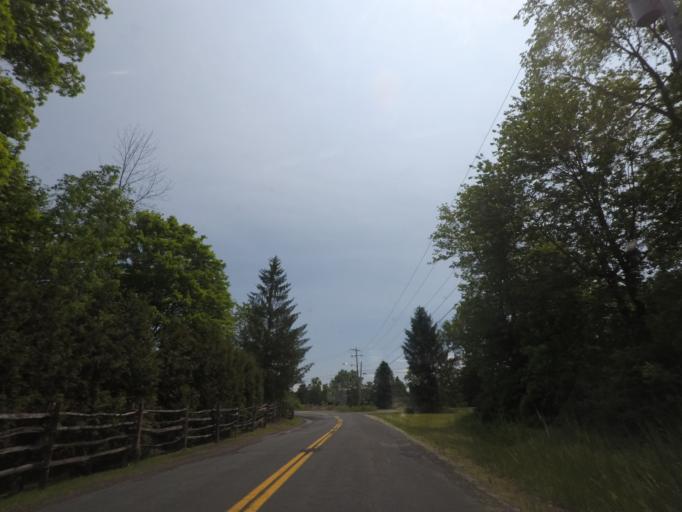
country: US
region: New York
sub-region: Columbia County
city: Niverville
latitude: 42.4764
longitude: -73.6953
